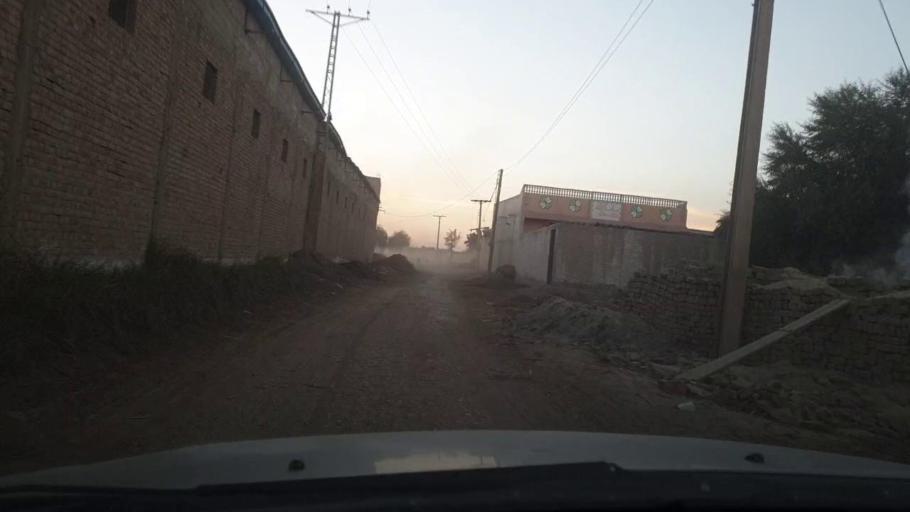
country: PK
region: Sindh
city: Ghotki
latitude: 27.9815
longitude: 69.2827
